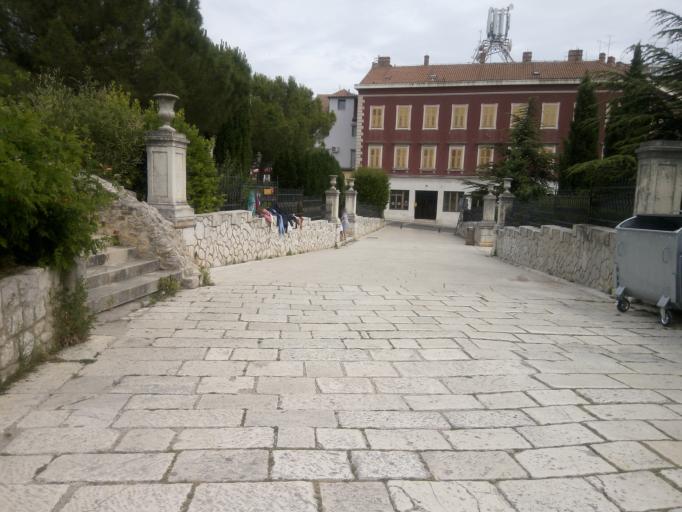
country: HR
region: Sibensko-Kniniska
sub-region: Grad Sibenik
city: Sibenik
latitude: 43.7339
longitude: 15.8924
